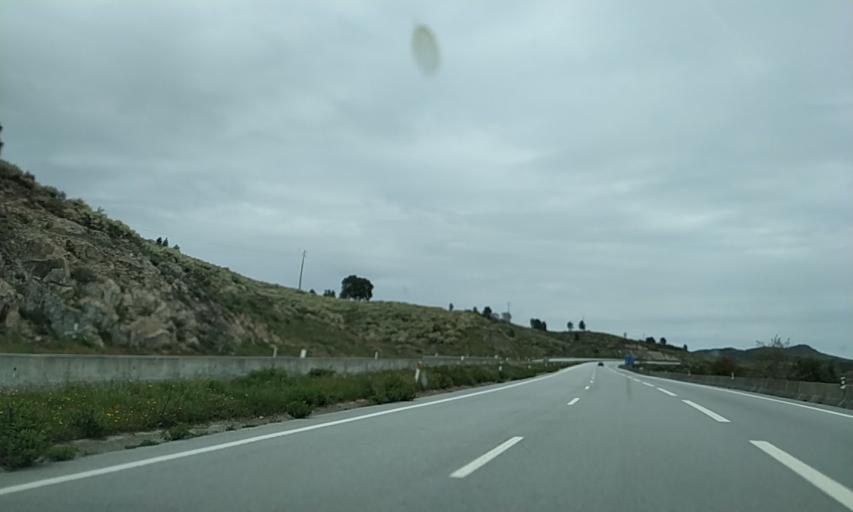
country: PT
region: Guarda
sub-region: Fornos de Algodres
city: Fornos de Algodres
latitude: 40.6308
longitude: -7.4690
